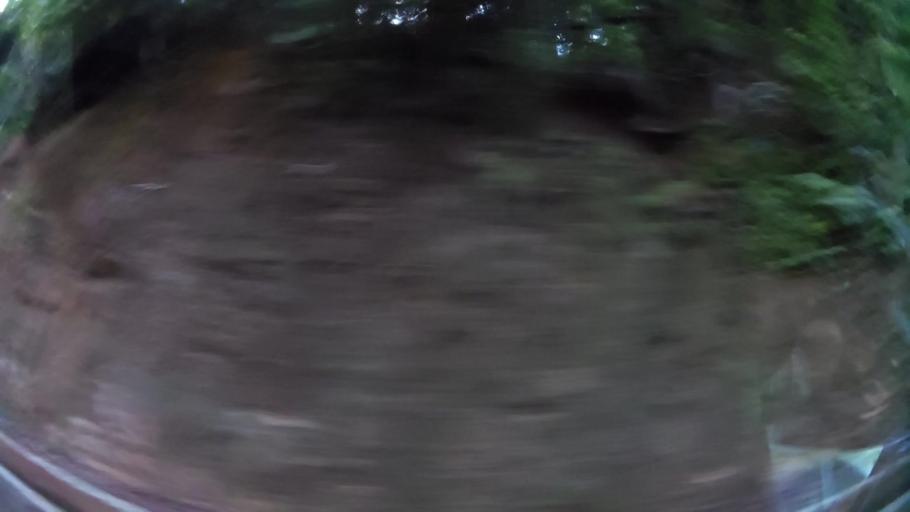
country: DM
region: Saint Andrew
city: Calibishie
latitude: 15.5892
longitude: -61.3991
